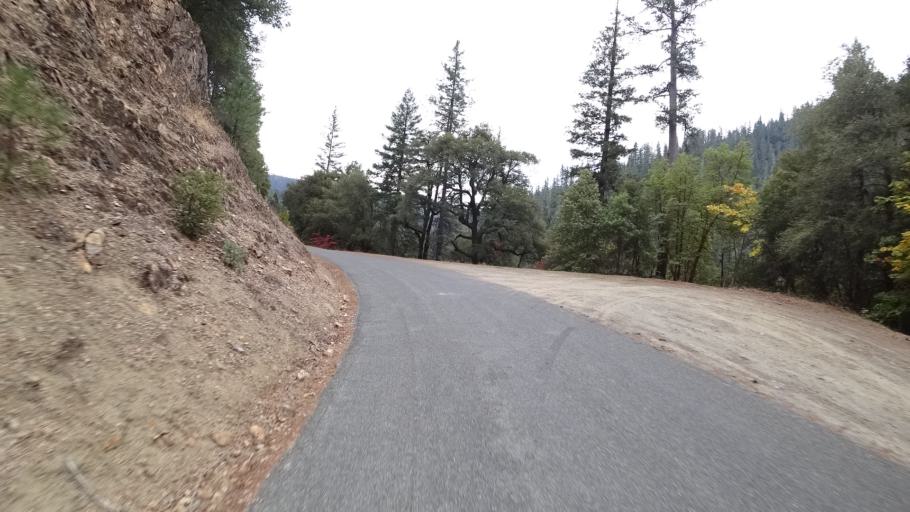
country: US
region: California
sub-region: Siskiyou County
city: Happy Camp
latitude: 41.7662
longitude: -123.3670
